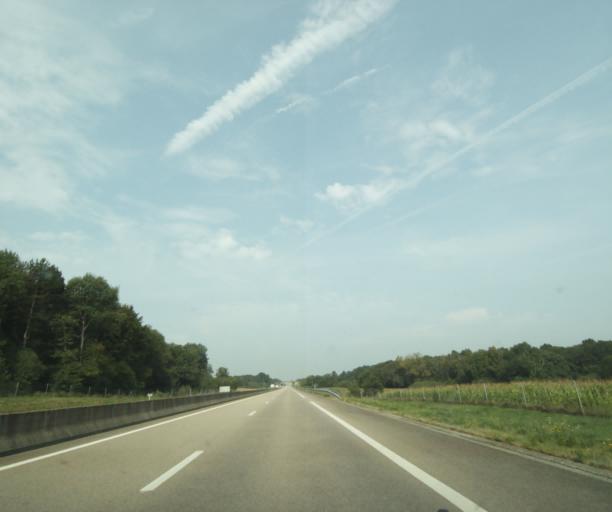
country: FR
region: Lower Normandy
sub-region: Departement du Calvados
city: Falaise
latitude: 48.8354
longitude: -0.1529
